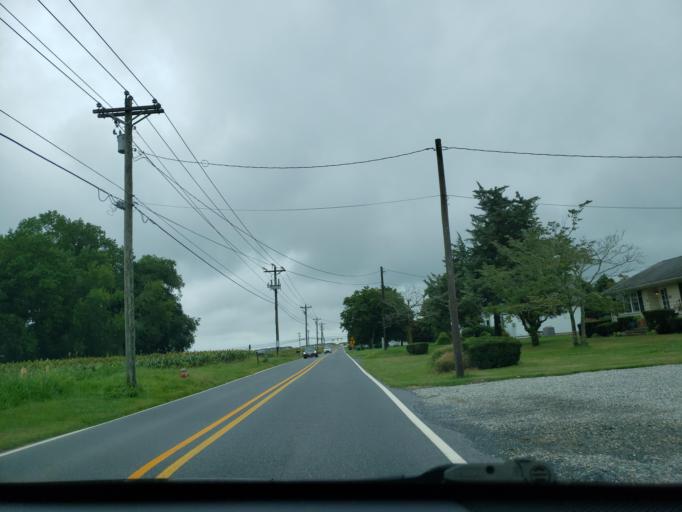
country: US
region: Delaware
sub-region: Sussex County
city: Lewes
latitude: 38.7518
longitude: -75.1536
